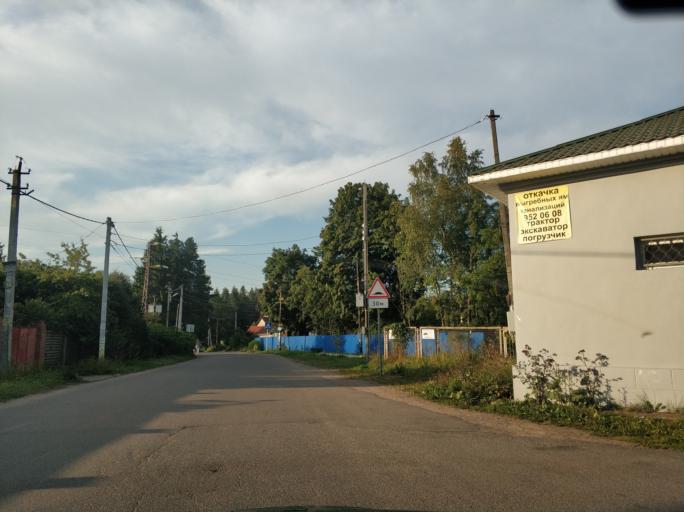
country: RU
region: Leningrad
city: Shcheglovo
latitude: 60.0533
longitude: 30.7442
